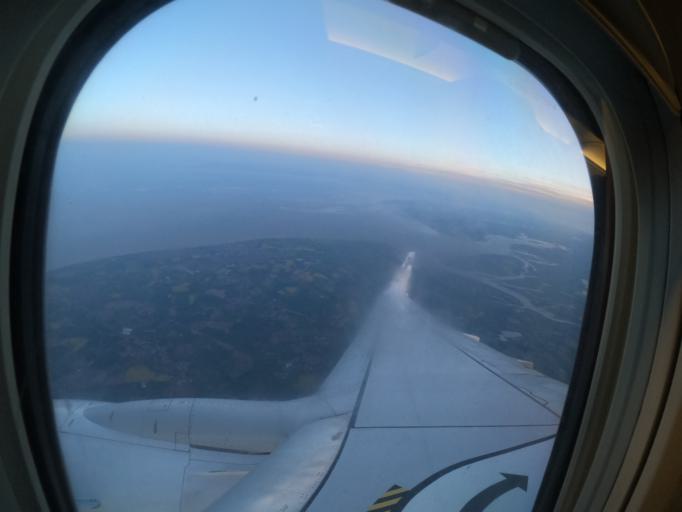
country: GB
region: England
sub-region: Essex
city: Mistley
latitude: 51.9053
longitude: 1.1298
